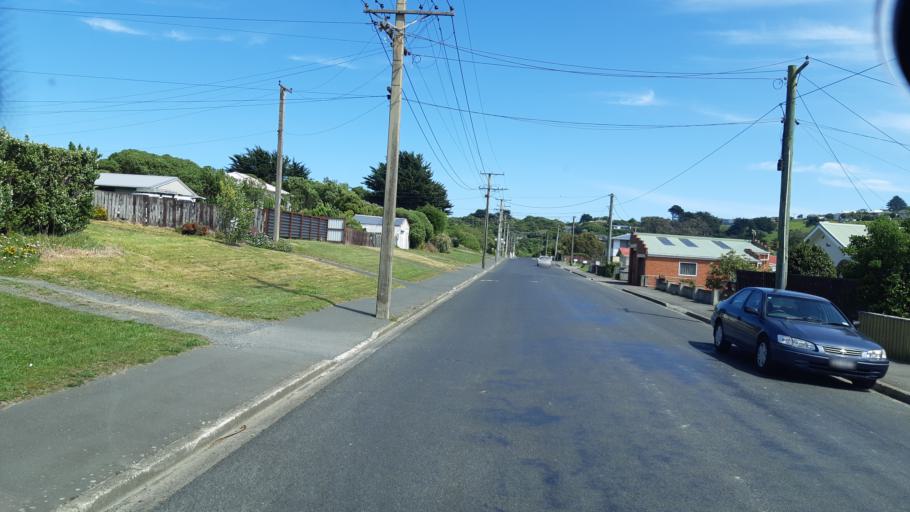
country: NZ
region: Otago
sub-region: Dunedin City
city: Dunedin
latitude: -45.9034
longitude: 170.5478
